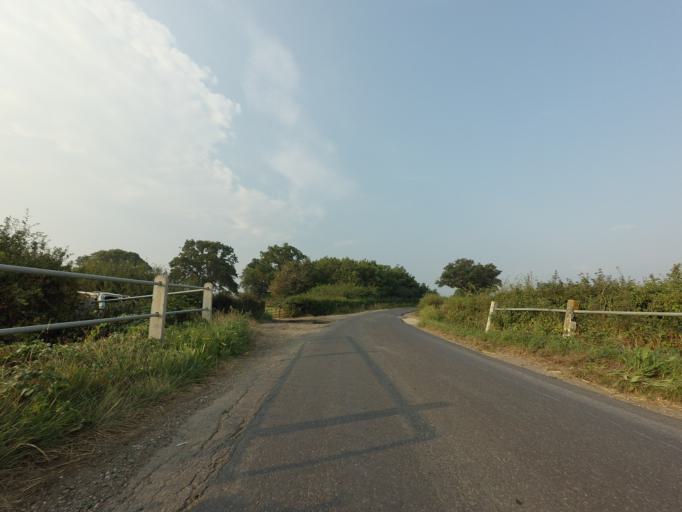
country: GB
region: England
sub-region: Kent
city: Ashford
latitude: 51.1181
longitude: 0.8233
